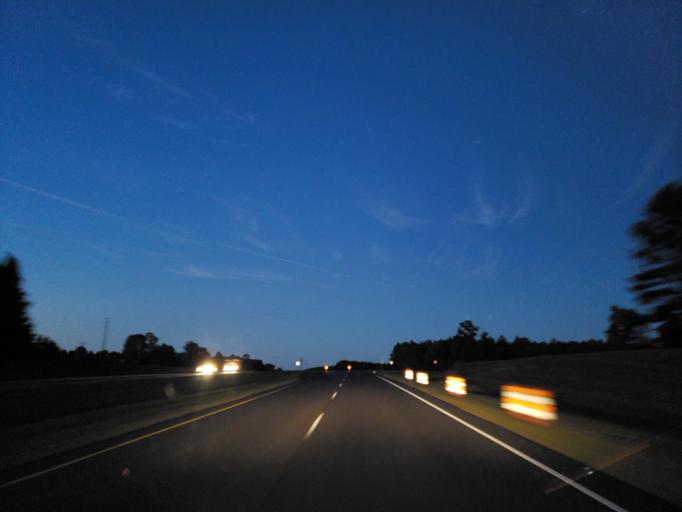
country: US
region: Mississippi
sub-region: Clarke County
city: Quitman
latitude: 32.0062
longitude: -88.6904
